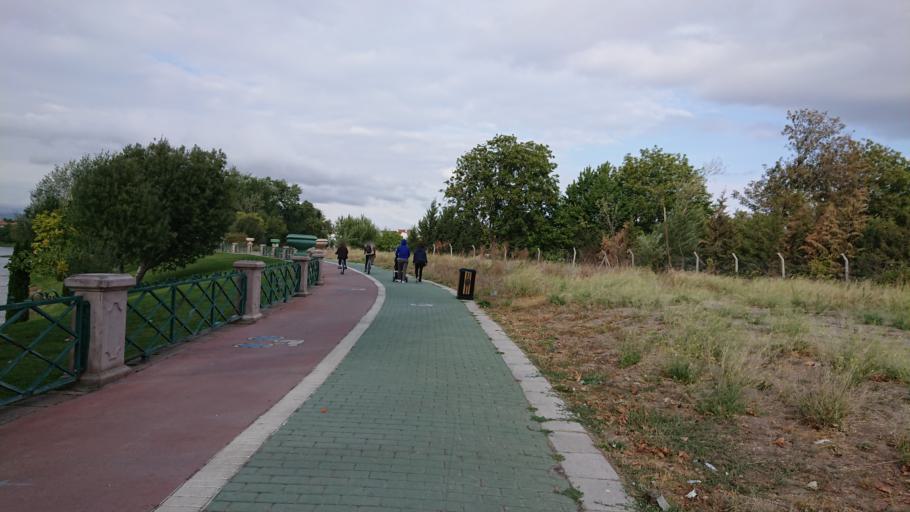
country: TR
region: Eskisehir
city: Eskisehir
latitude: 39.7601
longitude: 30.4847
